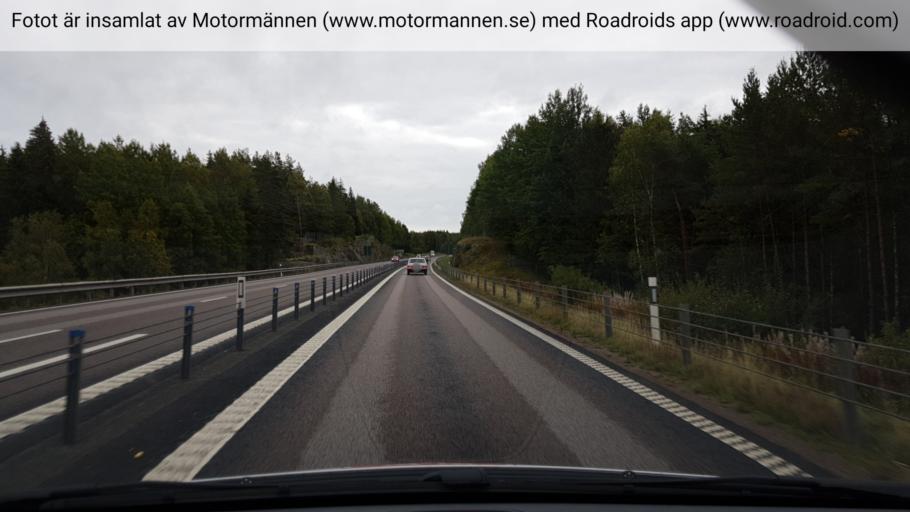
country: SE
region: Vaermland
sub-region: Karlstads Kommun
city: Skattkarr
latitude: 59.4206
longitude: 13.6971
